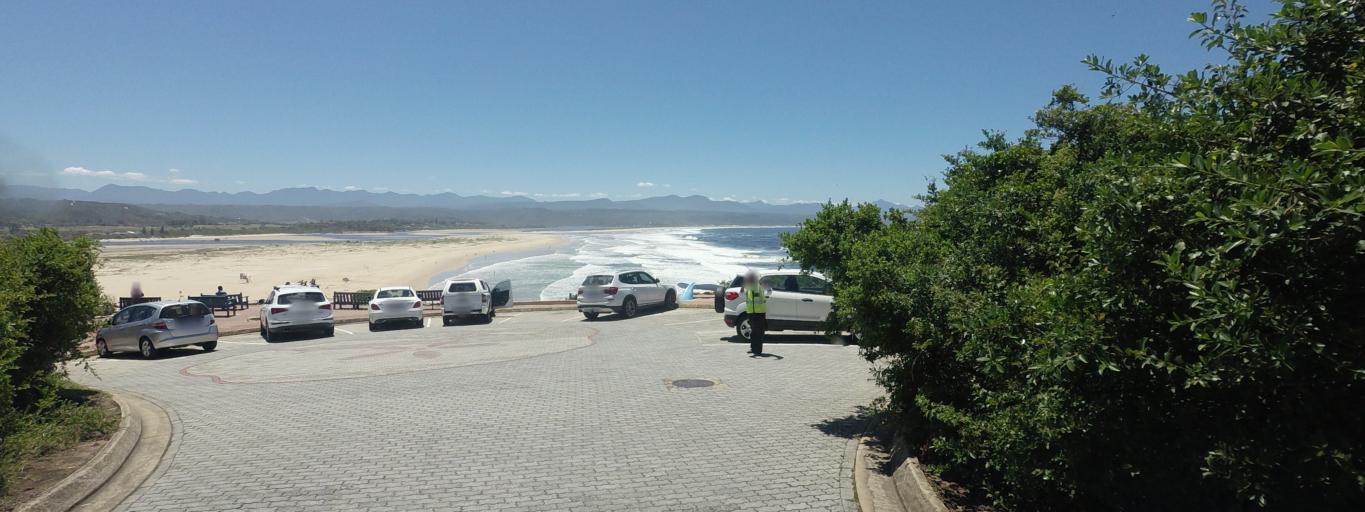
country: ZA
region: Western Cape
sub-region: Eden District Municipality
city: Plettenberg Bay
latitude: -34.0530
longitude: 23.3777
